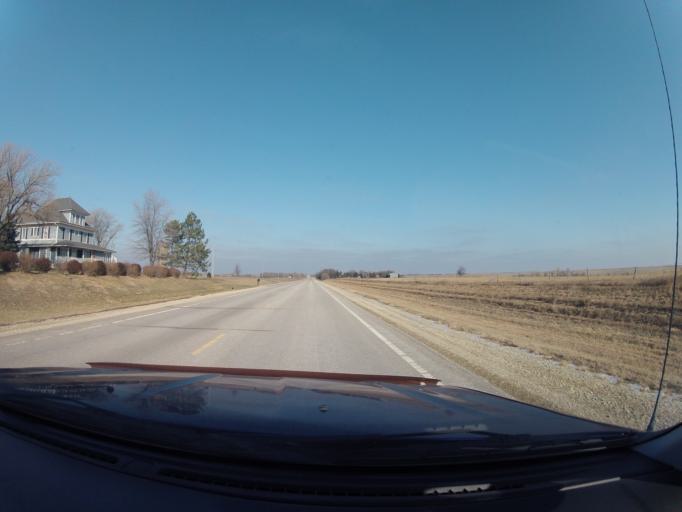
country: US
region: Kansas
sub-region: Marshall County
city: Blue Rapids
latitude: 39.6056
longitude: -96.7501
